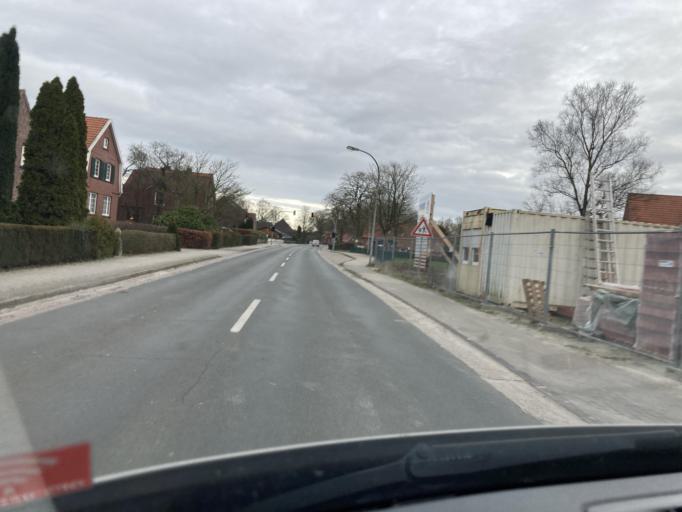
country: DE
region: Lower Saxony
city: Leer
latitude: 53.1634
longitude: 7.4574
